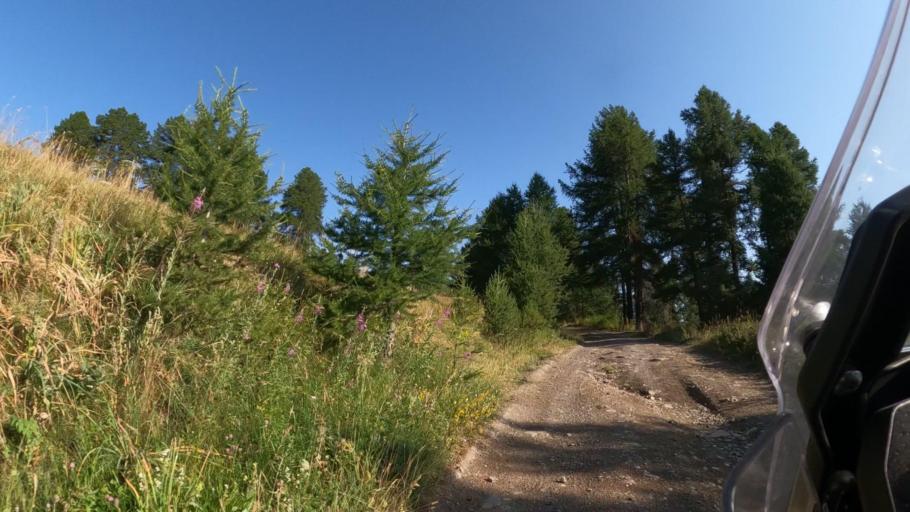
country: FR
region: Provence-Alpes-Cote d'Azur
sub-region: Departement des Hautes-Alpes
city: Guillestre
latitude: 44.6085
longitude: 6.6686
